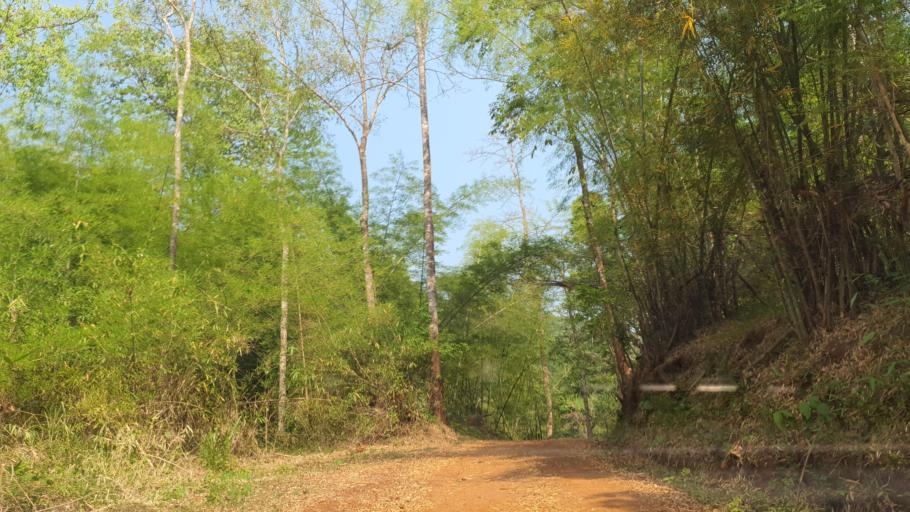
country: TH
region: Chiang Mai
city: Samoeng
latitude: 18.7948
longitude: 98.7954
